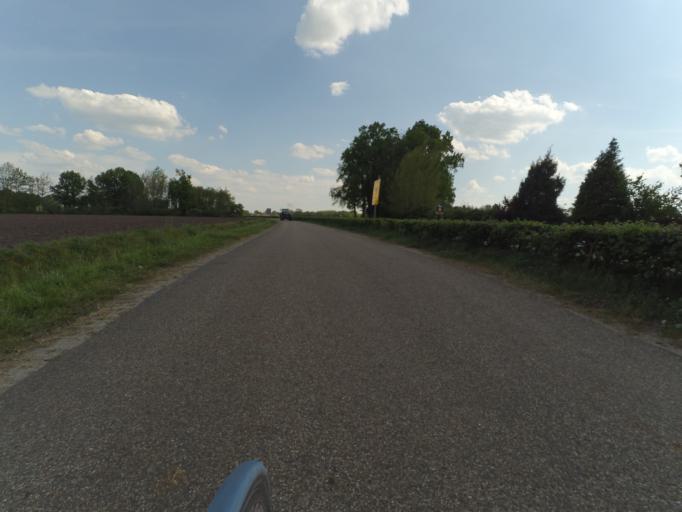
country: NL
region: Overijssel
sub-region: Gemeente Oldenzaal
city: Oldenzaal
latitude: 52.3426
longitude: 6.8638
